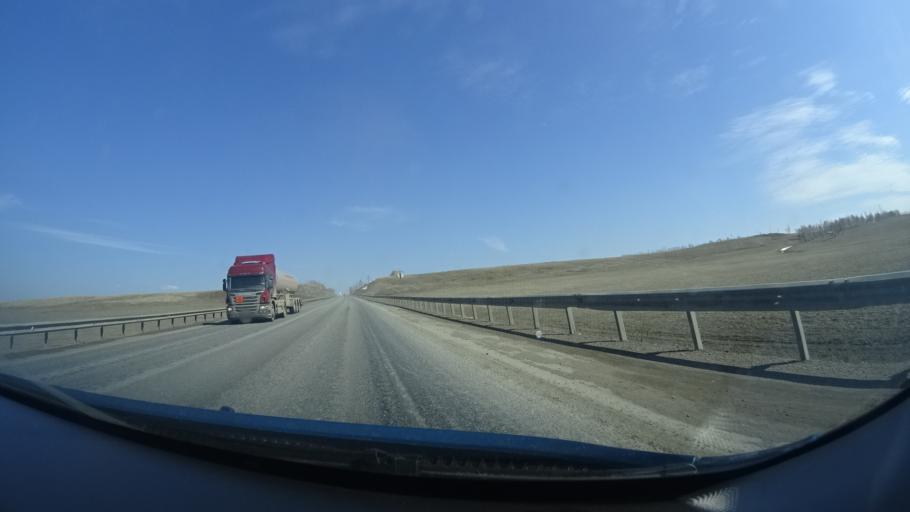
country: RU
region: Bashkortostan
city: Serafimovskiy
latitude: 54.4585
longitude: 53.7209
